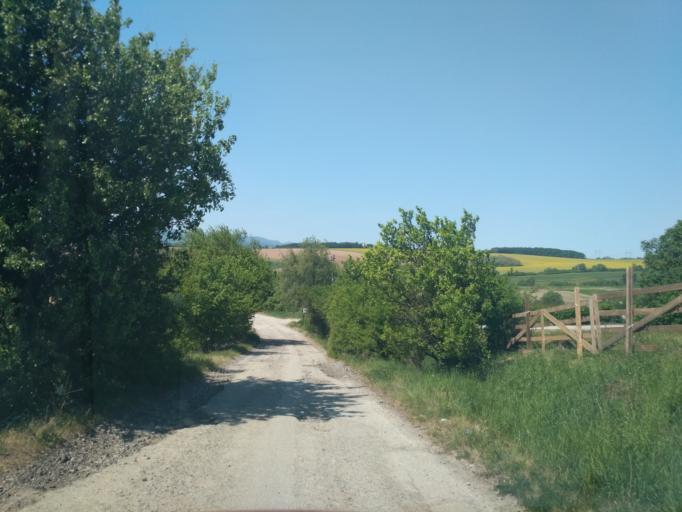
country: SK
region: Kosicky
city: Kosice
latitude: 48.7925
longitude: 21.3639
